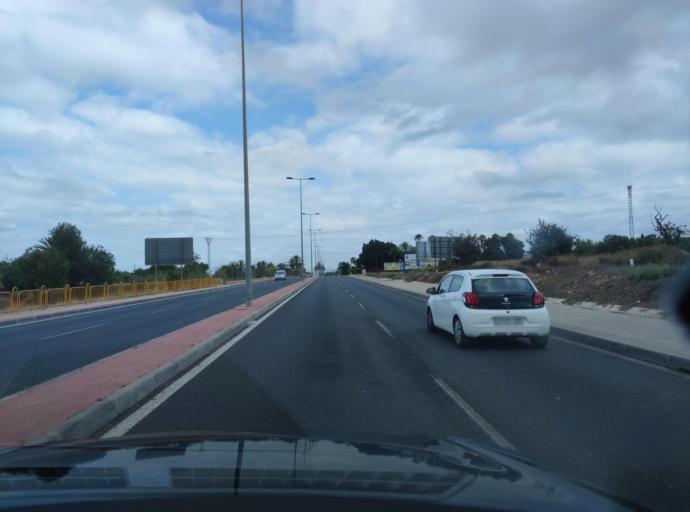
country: ES
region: Valencia
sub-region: Provincia de Alicante
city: Santa Pola
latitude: 38.2023
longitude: -0.5738
